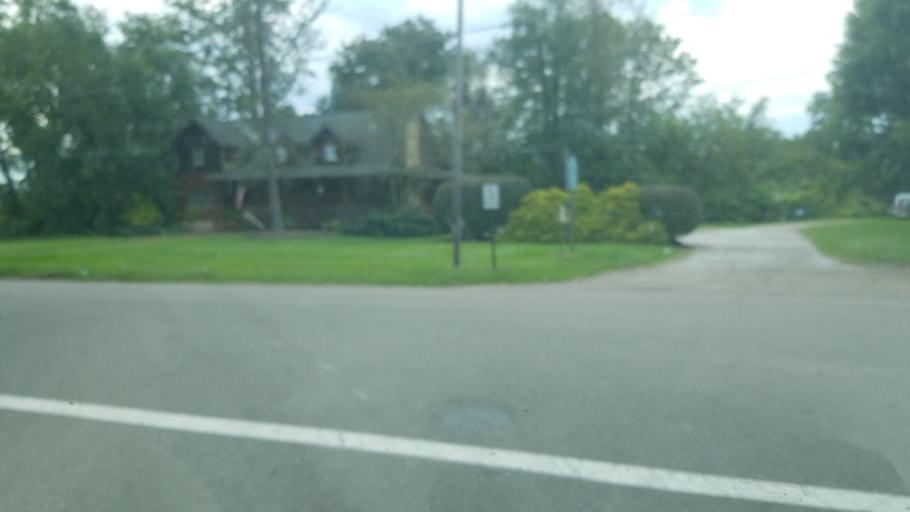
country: US
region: Ohio
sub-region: Carroll County
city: Lake Mohawk
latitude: 40.6546
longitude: -81.2986
